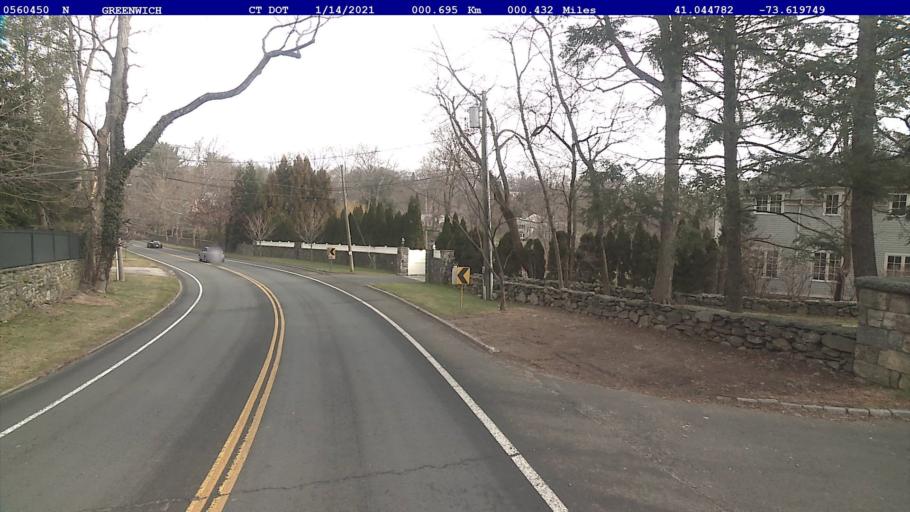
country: US
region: Connecticut
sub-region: Fairfield County
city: Greenwich
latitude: 41.0448
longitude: -73.6198
